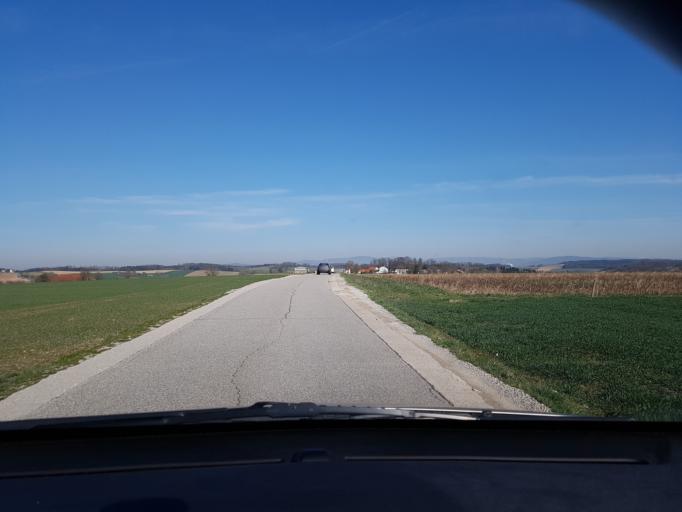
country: AT
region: Upper Austria
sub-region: Politischer Bezirk Linz-Land
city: Ansfelden
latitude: 48.1560
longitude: 14.3088
